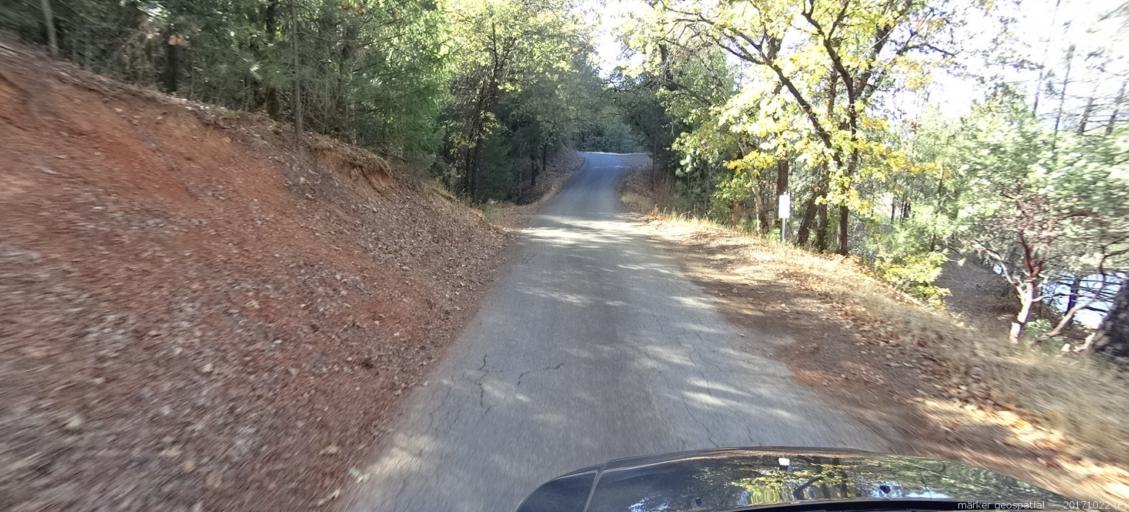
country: US
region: California
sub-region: Shasta County
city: Shasta Lake
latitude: 40.8419
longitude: -122.3545
